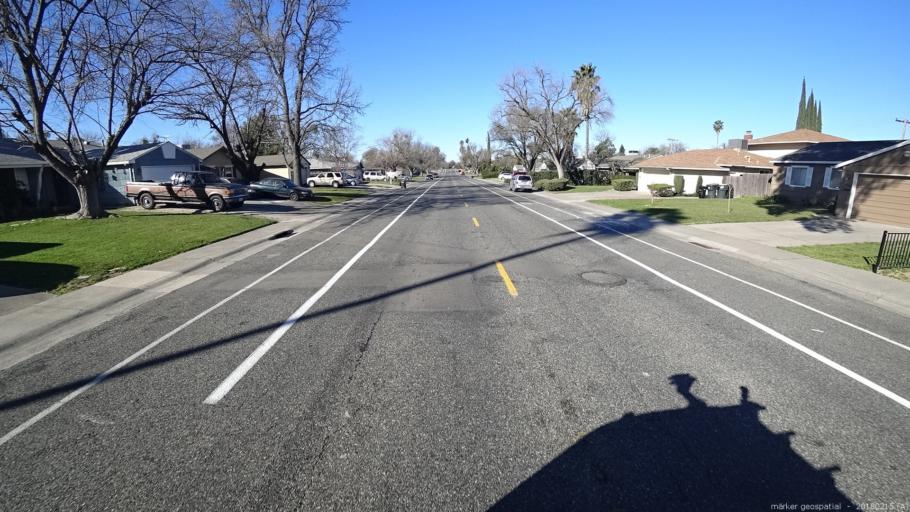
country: US
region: California
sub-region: Sacramento County
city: Foothill Farms
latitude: 38.6658
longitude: -121.3129
